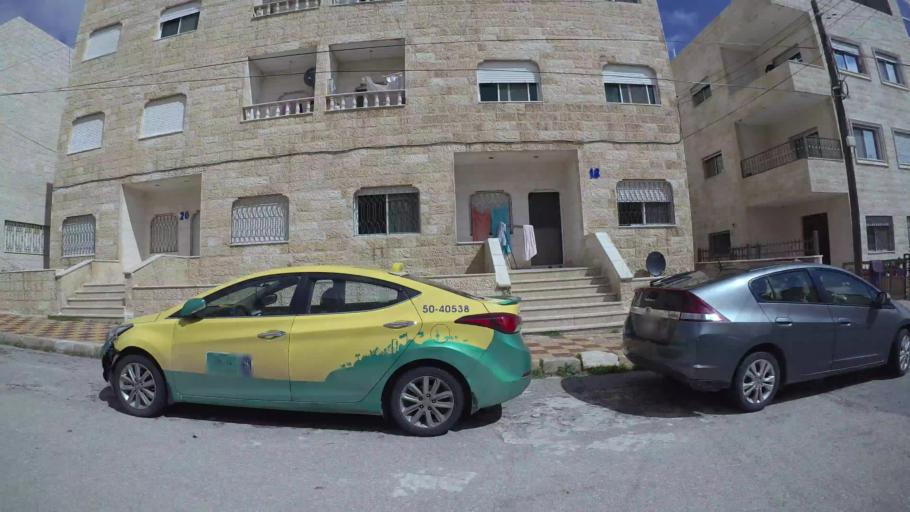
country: JO
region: Amman
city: Al Jubayhah
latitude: 32.0597
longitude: 35.8742
